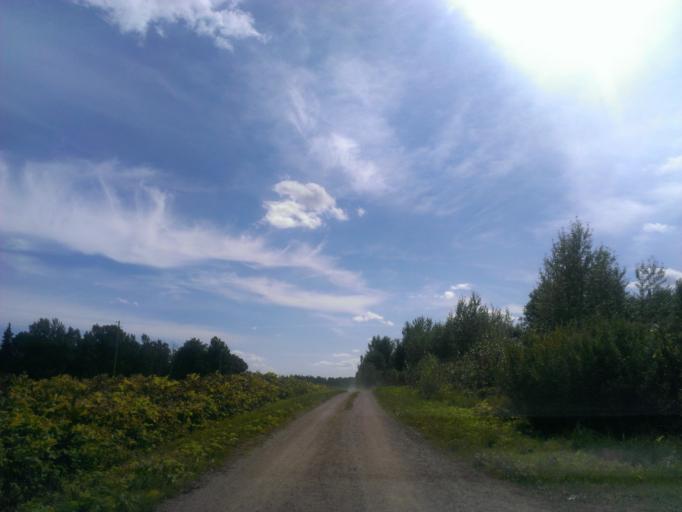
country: LV
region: Ligatne
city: Ligatne
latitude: 57.2298
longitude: 24.9579
